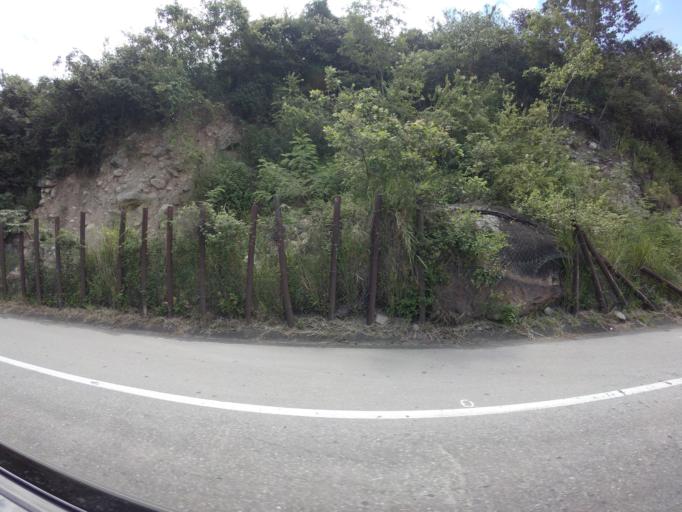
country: CO
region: Tolima
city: Icononzo
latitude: 4.2583
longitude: -74.5419
